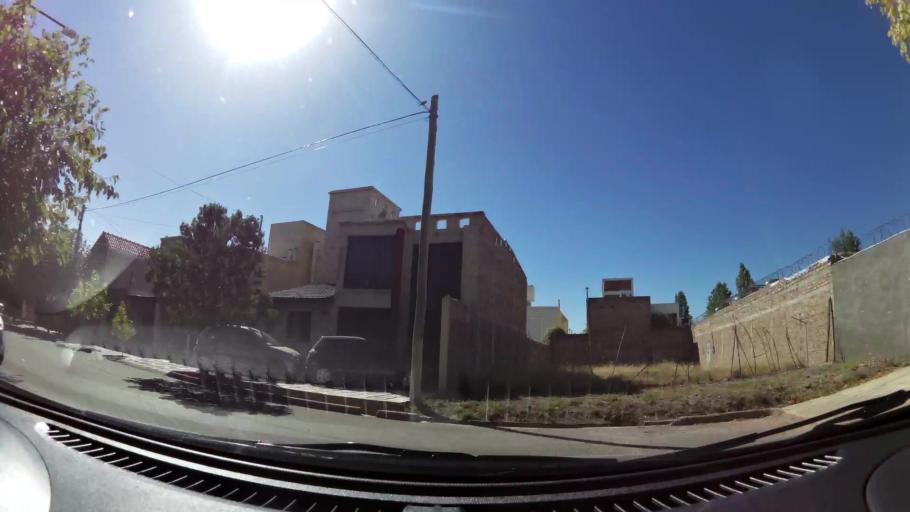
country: AR
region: Mendoza
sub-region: Departamento de Maipu
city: Maipu
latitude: -32.9749
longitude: -68.7992
